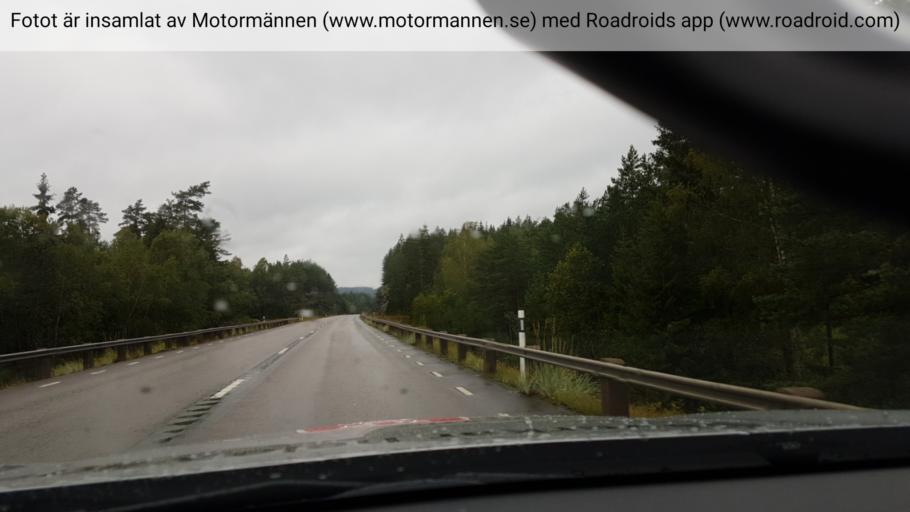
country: SE
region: Vaestra Goetaland
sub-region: Bengtsfors Kommun
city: Billingsfors
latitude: 58.9301
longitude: 12.1680
